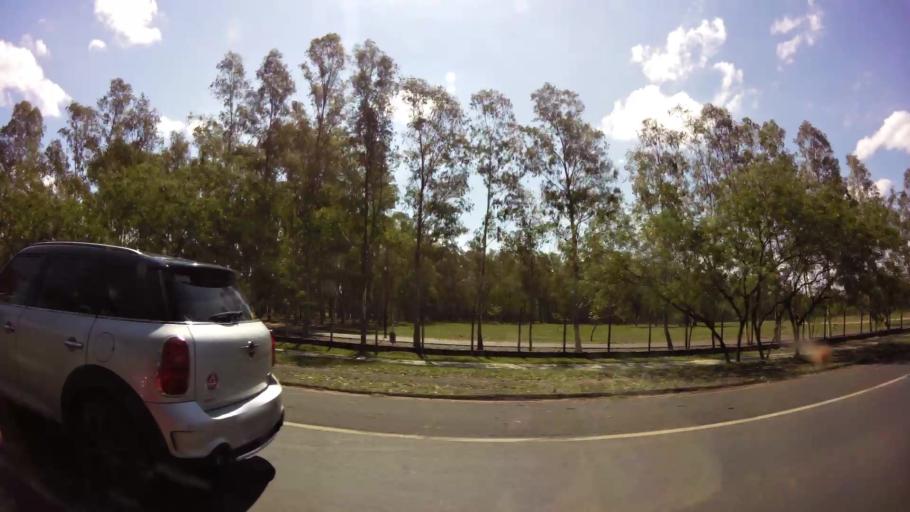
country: PY
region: Central
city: Fernando de la Mora
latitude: -25.2641
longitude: -57.5344
